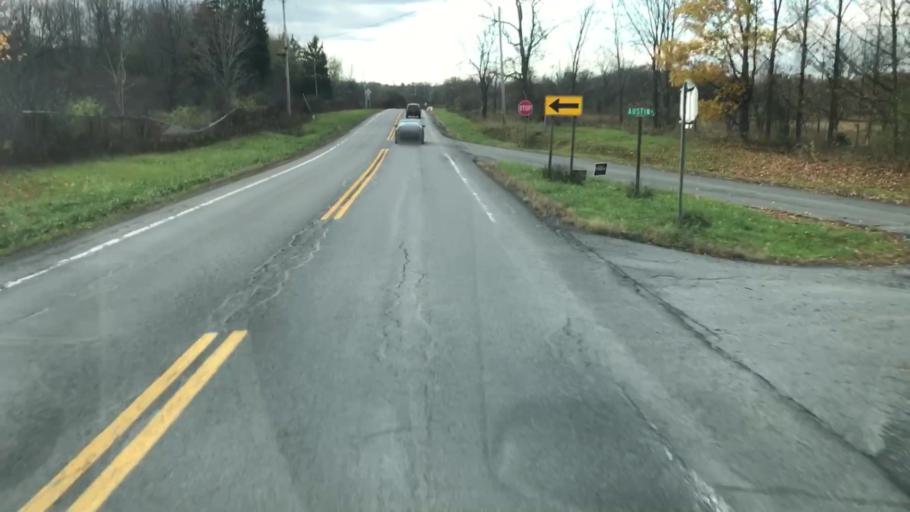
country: US
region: New York
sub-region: Onondaga County
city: Elbridge
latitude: 43.0004
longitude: -76.4250
